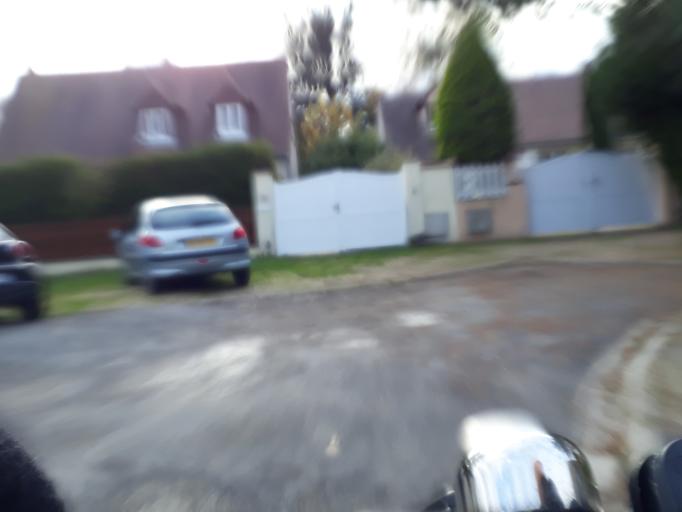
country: FR
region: Ile-de-France
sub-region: Departement de Seine-et-Marne
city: Bois-le-Roi
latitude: 48.4676
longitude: 2.6926
